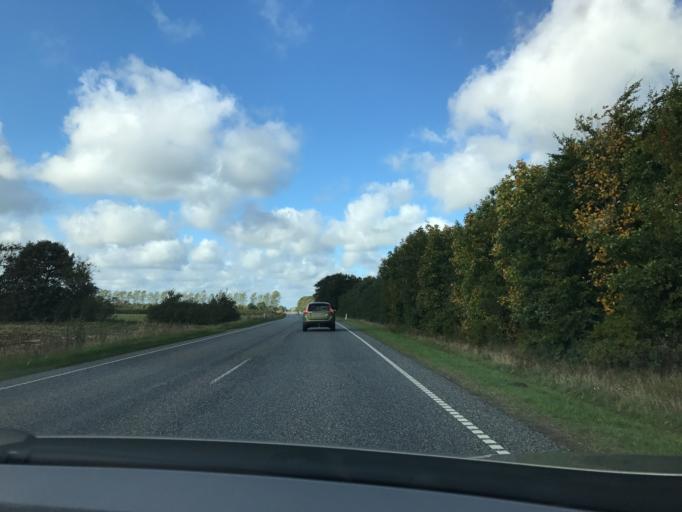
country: DK
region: South Denmark
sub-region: Billund Kommune
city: Billund
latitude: 55.7175
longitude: 9.1815
